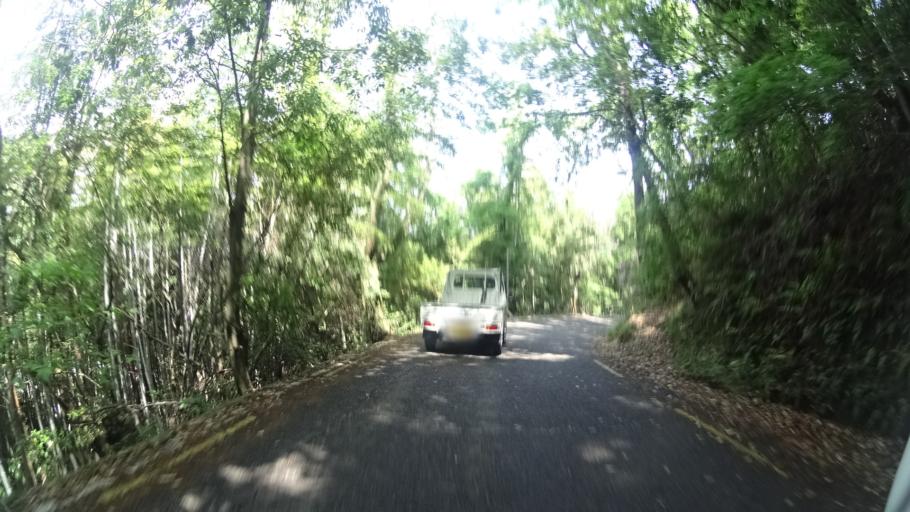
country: JP
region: Tokushima
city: Tokushima-shi
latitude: 34.0704
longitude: 134.5133
